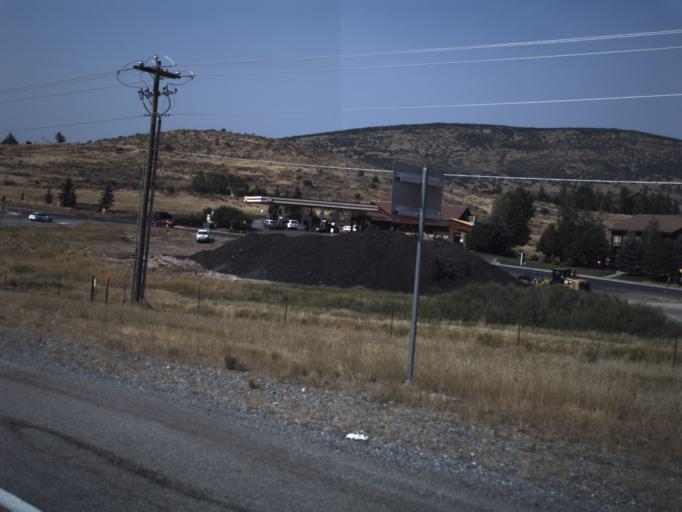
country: US
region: Utah
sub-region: Summit County
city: Summit Park
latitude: 40.7538
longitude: -111.5708
